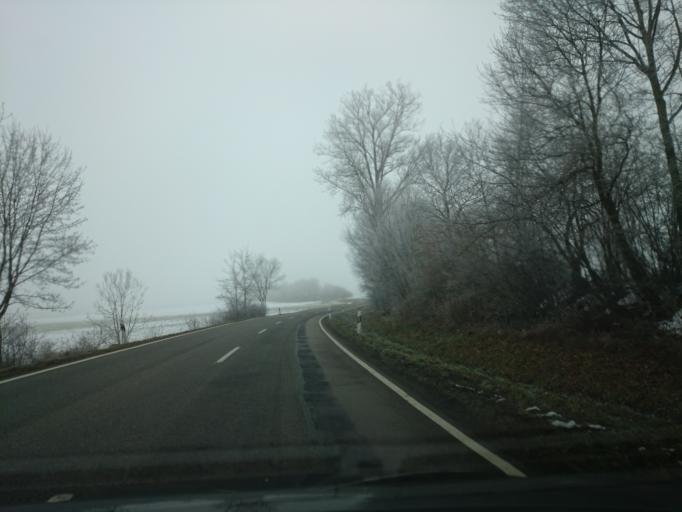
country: DE
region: Bavaria
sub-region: Regierungsbezirk Mittelfranken
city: Thalmassing
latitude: 49.1407
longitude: 11.2632
